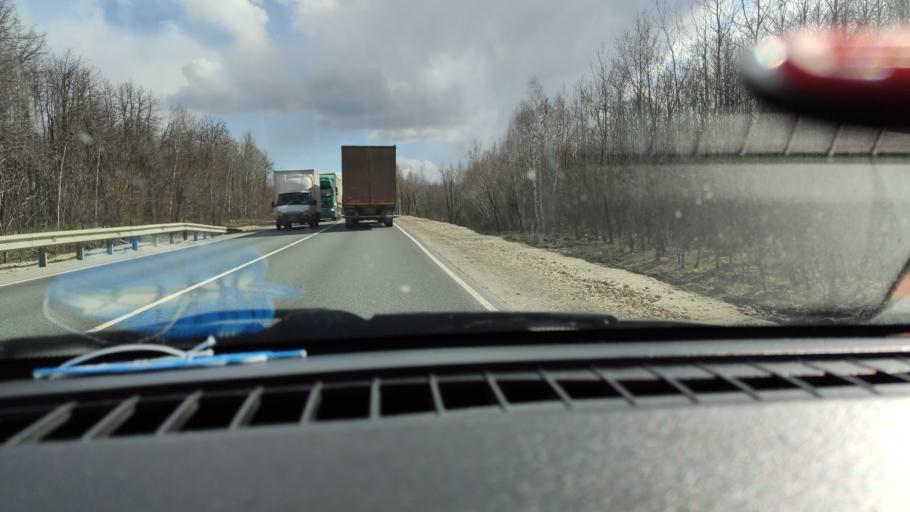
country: RU
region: Saratov
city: Khvalynsk
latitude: 52.4752
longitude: 48.0139
